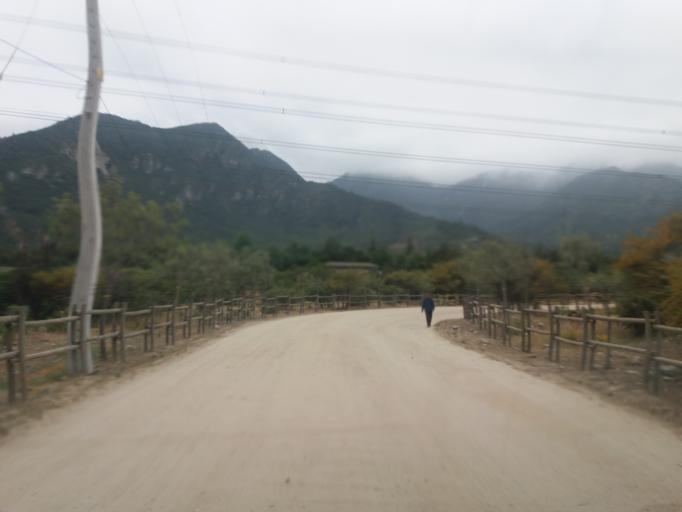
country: CL
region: Valparaiso
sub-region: Provincia de Marga Marga
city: Limache
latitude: -33.0278
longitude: -71.1413
